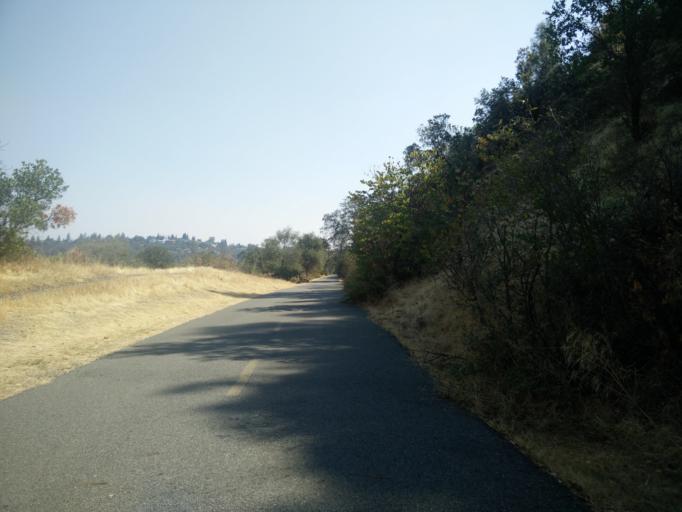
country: US
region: California
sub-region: Shasta County
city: Shasta
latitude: 40.5986
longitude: -122.4432
